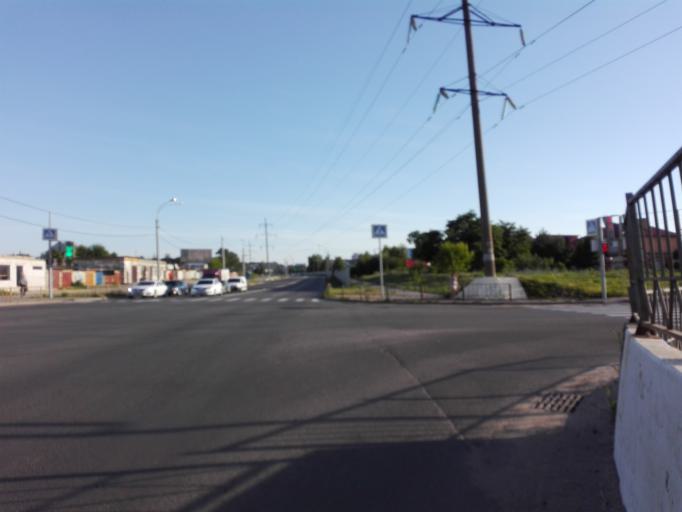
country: RU
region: Orjol
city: Orel
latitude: 52.9583
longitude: 36.0321
